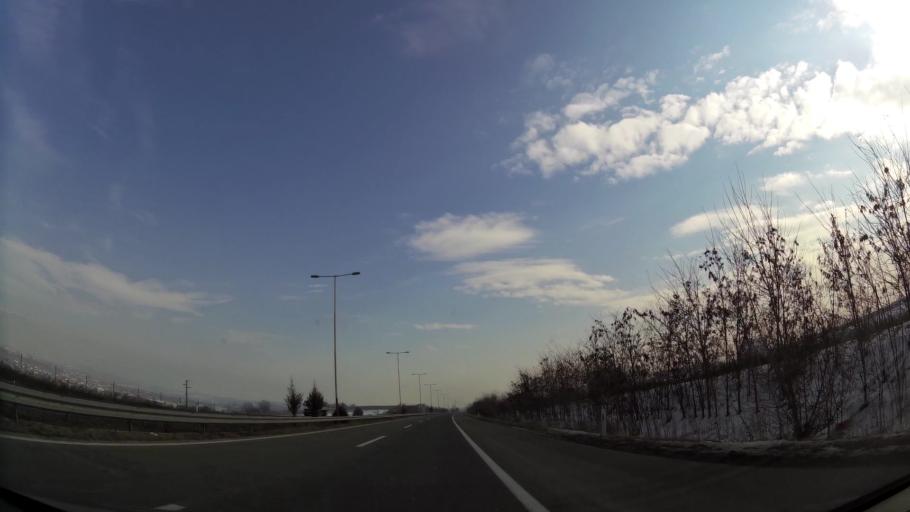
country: MK
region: Suto Orizari
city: Suto Orizare
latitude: 42.0507
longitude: 21.4296
